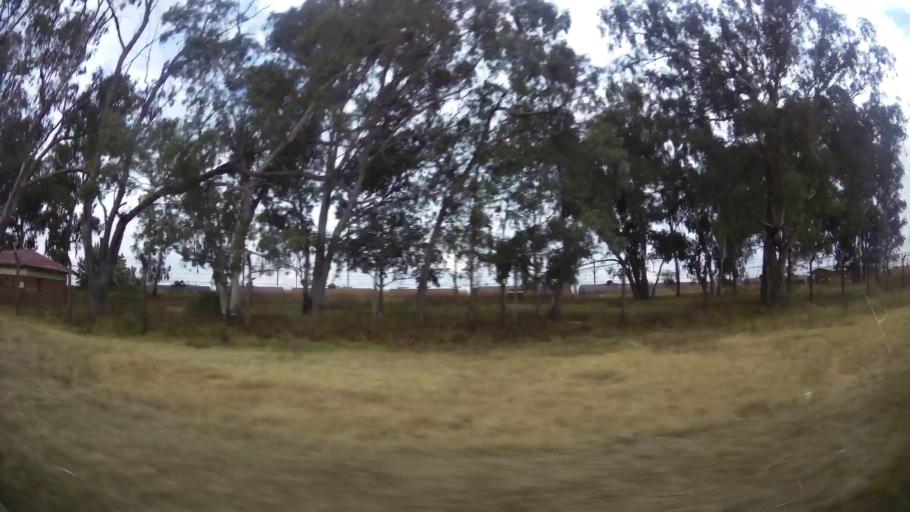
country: ZA
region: Orange Free State
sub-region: Fezile Dabi District Municipality
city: Sasolburg
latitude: -26.8505
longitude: 27.8670
